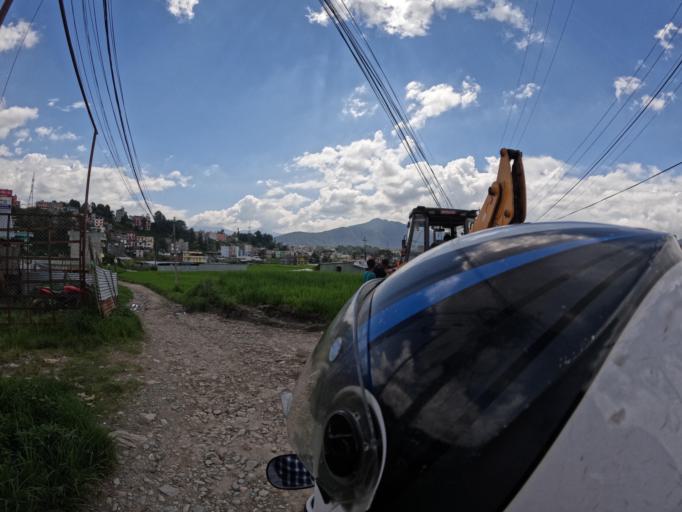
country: NP
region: Central Region
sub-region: Bagmati Zone
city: Kathmandu
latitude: 27.7650
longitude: 85.3258
